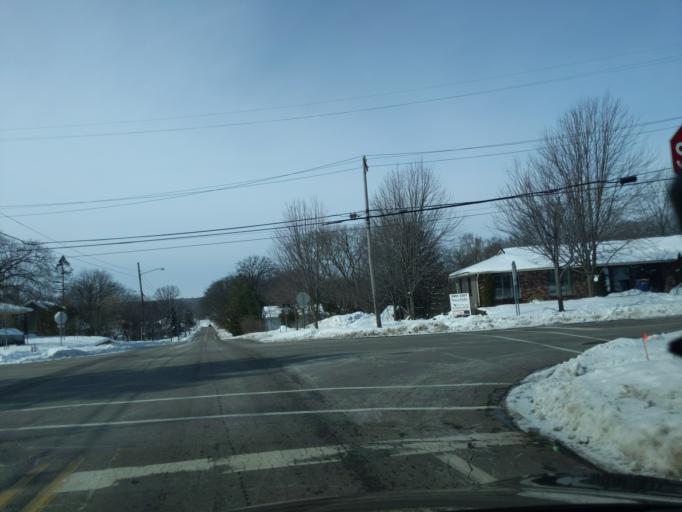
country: US
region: Michigan
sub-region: Kent County
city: Comstock Park
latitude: 43.0136
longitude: -85.6571
